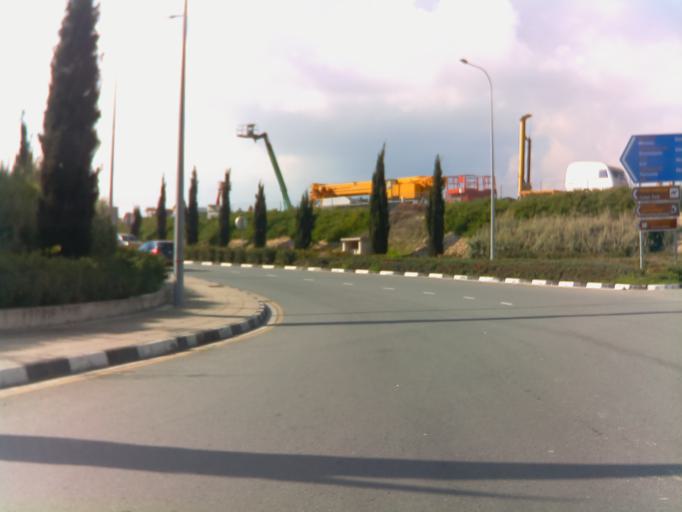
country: CY
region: Larnaka
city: Dhromolaxia
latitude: 34.8753
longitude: 33.6025
